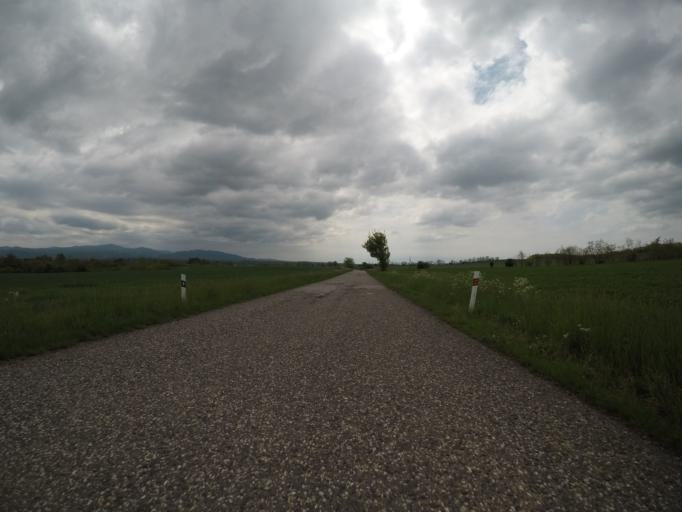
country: SK
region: Nitriansky
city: Sahy
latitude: 48.0827
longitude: 18.8660
